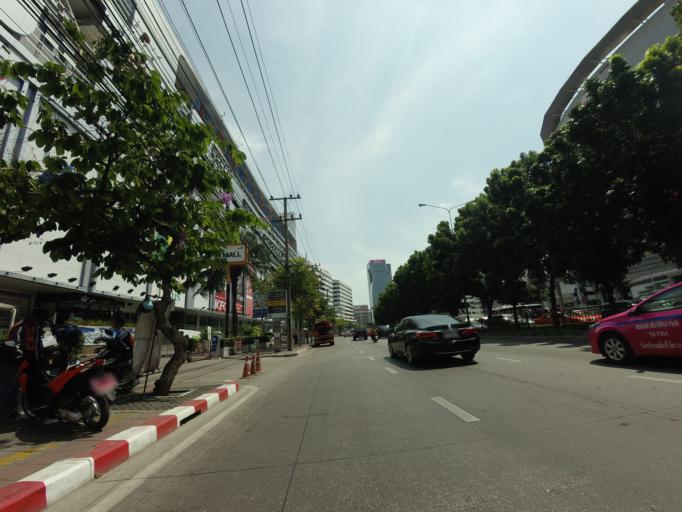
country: TH
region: Bangkok
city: Din Daeng
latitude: 13.7593
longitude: 100.5656
